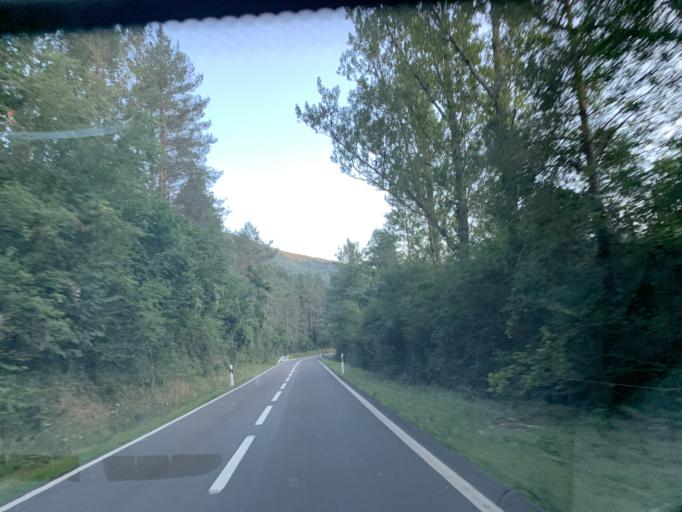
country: ES
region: Aragon
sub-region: Provincia de Huesca
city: Broto
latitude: 42.5607
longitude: -0.1169
